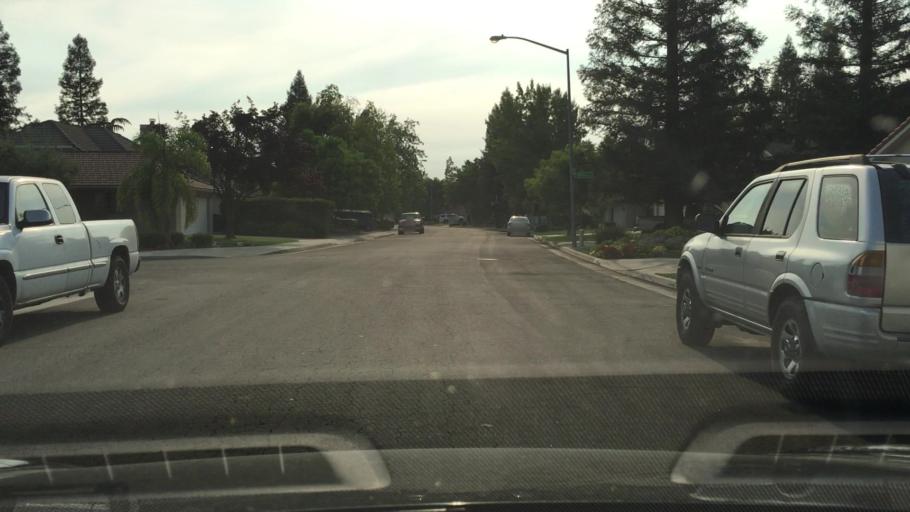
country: US
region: California
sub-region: Fresno County
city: Clovis
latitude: 36.8714
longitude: -119.7429
